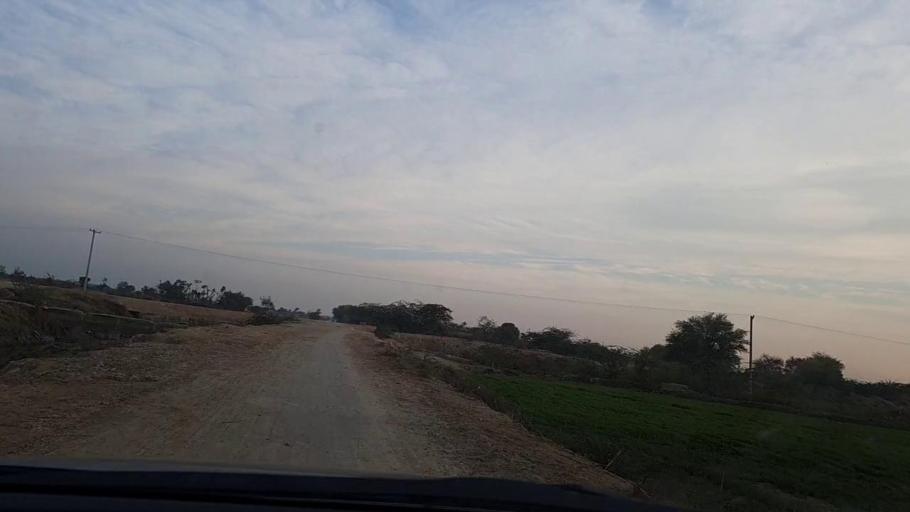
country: PK
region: Sindh
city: Sakrand
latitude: 26.1864
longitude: 68.3381
